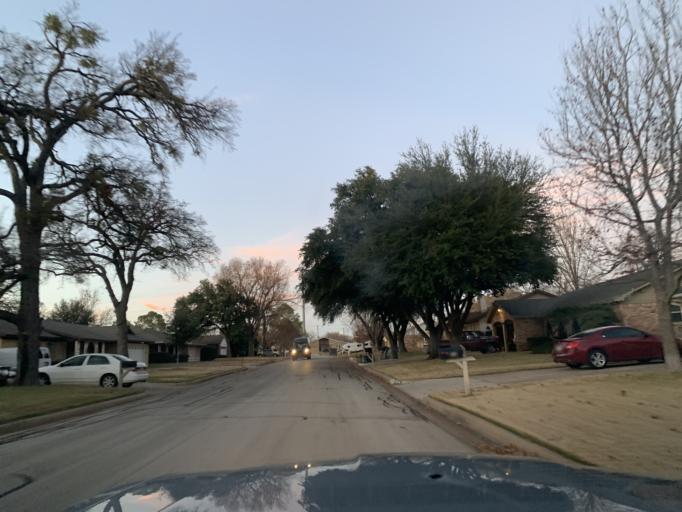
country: US
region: Texas
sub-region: Tarrant County
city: Bedford
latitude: 32.8500
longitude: -97.1520
